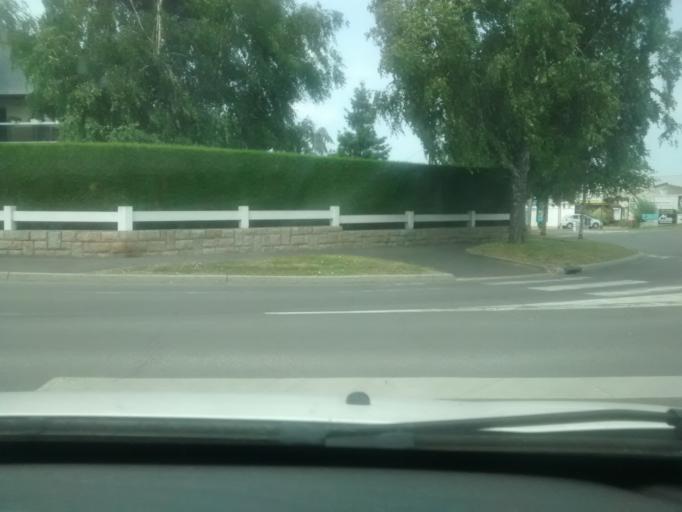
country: FR
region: Brittany
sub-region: Departement d'Ille-et-Vilaine
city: Dinard
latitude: 48.6269
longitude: -2.0737
